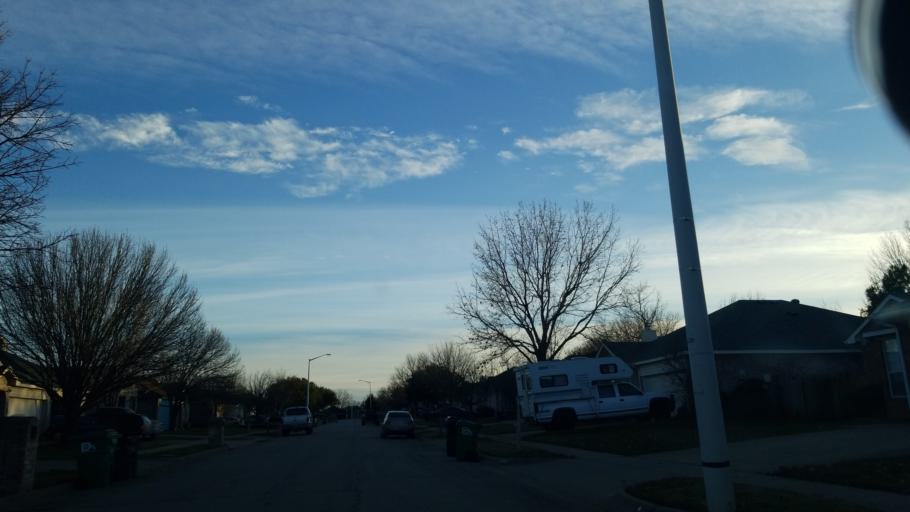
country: US
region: Texas
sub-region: Denton County
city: Corinth
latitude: 33.1614
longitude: -97.1088
